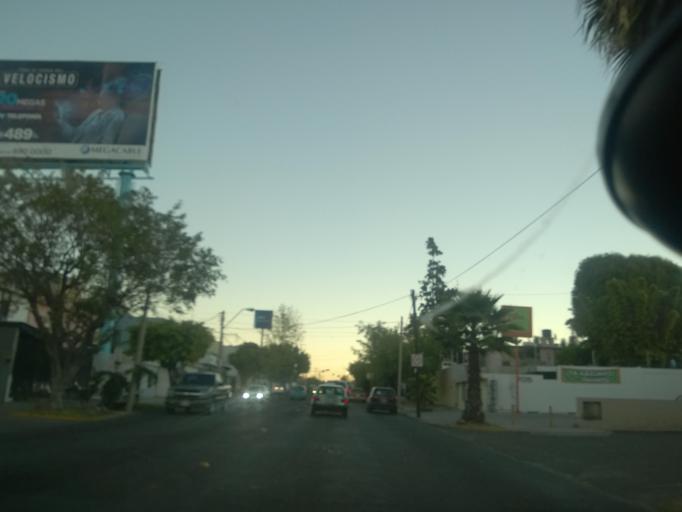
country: MX
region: Guanajuato
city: Leon
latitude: 21.1203
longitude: -101.6948
